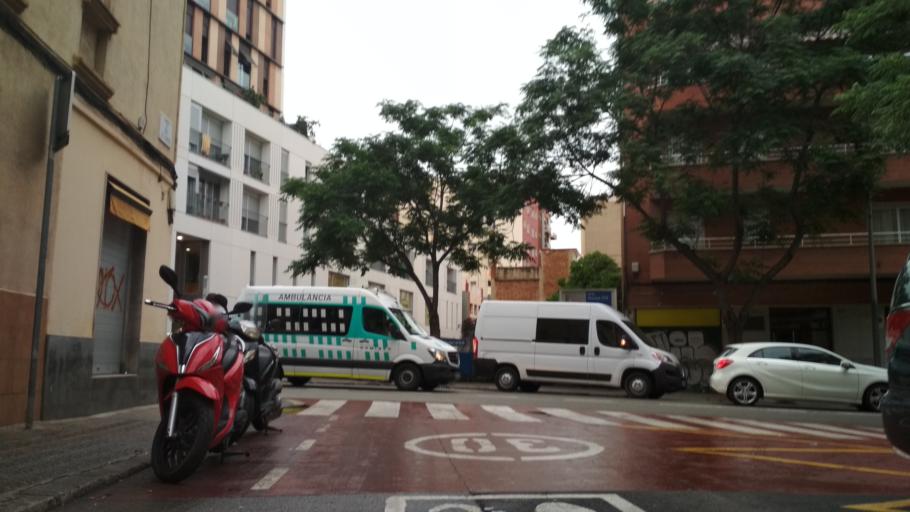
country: ES
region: Catalonia
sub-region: Provincia de Barcelona
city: Sant Marti
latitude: 41.4165
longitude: 2.1850
